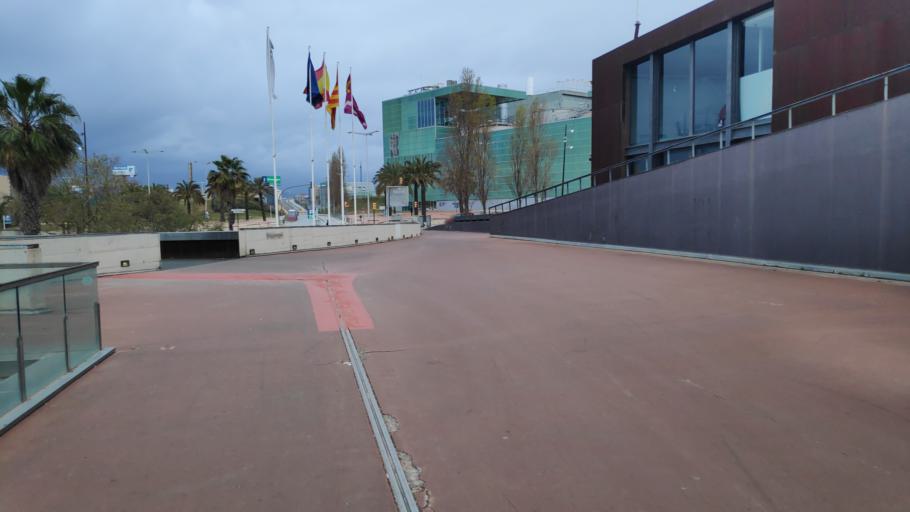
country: ES
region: Catalonia
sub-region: Provincia de Barcelona
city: Sant Adria de Besos
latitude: 41.4157
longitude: 2.2281
